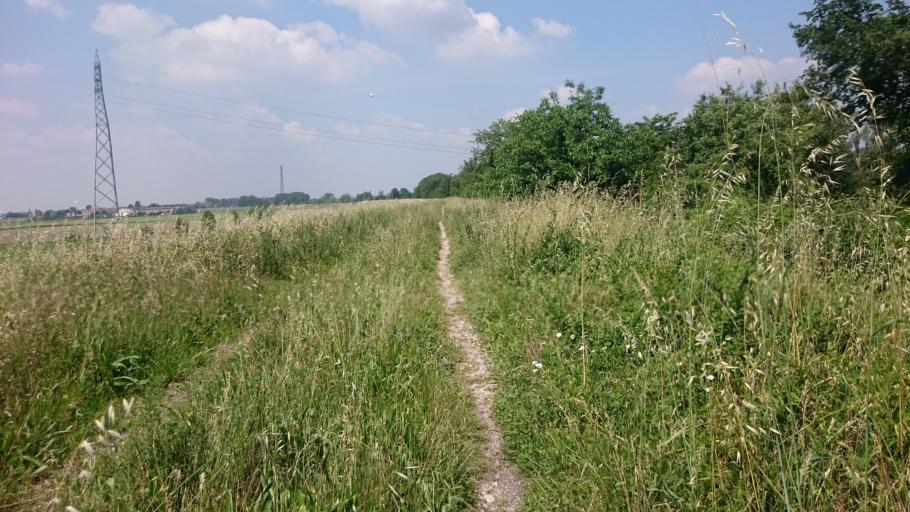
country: IT
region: Lombardy
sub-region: Provincia di Mantova
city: San Biagio
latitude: 45.1226
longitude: 10.8513
